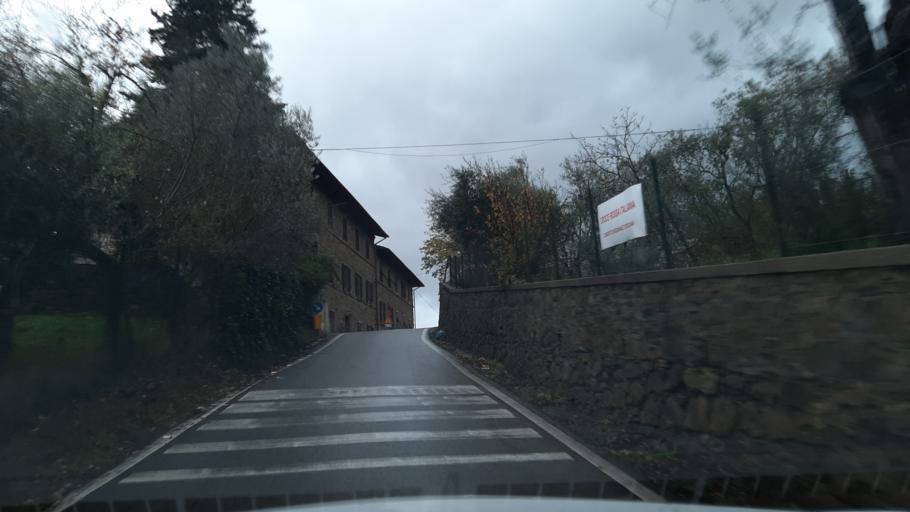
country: IT
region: Tuscany
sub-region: Province of Florence
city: Fiesole
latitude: 43.8075
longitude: 11.2674
